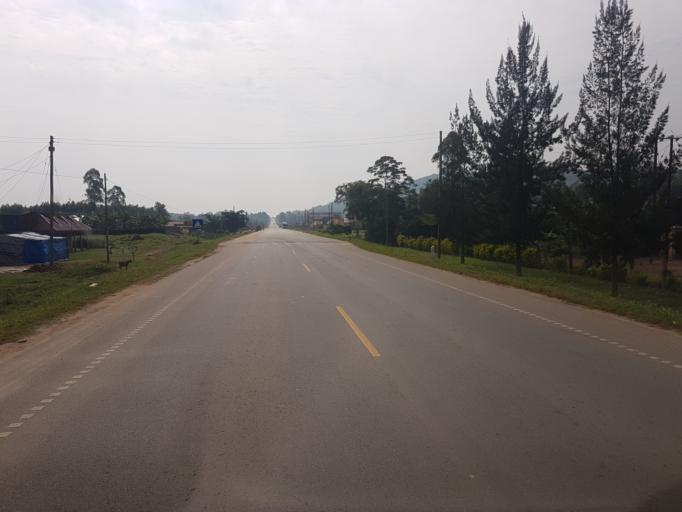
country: UG
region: Western Region
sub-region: Sheema District
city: Kibingo
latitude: -0.6432
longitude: 30.5004
